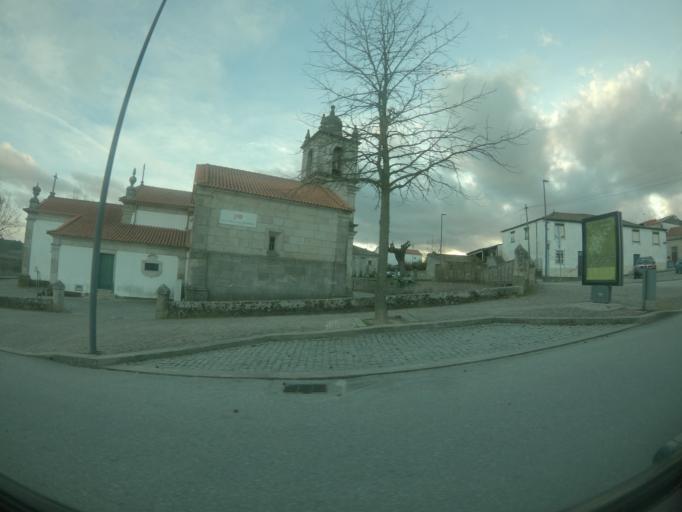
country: PT
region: Braganca
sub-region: Carrazeda de Ansiaes
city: Carrazeda de Anciaes
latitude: 41.2433
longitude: -7.3018
